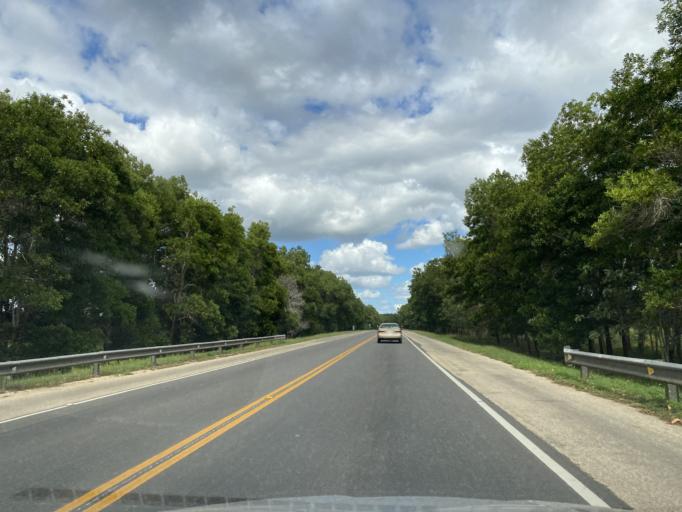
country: DO
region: Santo Domingo
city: Guerra
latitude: 18.6520
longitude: -69.7506
